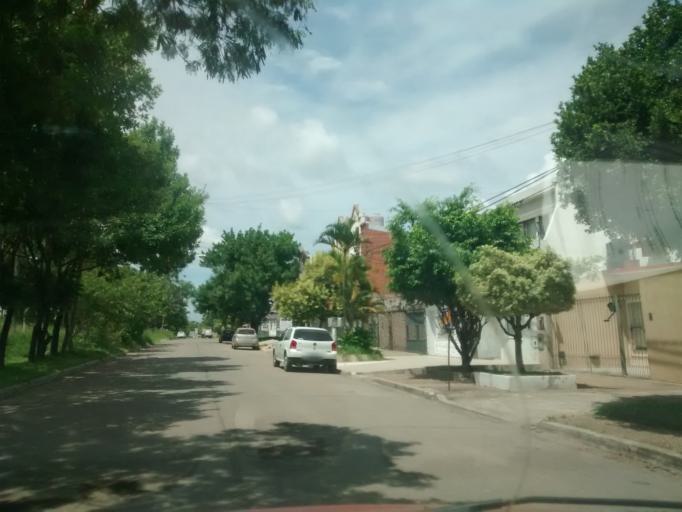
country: AR
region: Chaco
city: Resistencia
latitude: -27.4450
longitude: -58.9957
